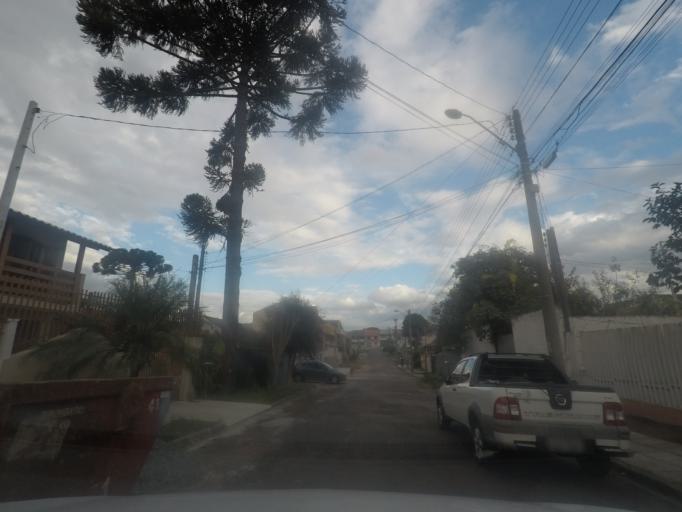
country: BR
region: Parana
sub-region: Pinhais
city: Pinhais
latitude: -25.4665
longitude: -49.2190
